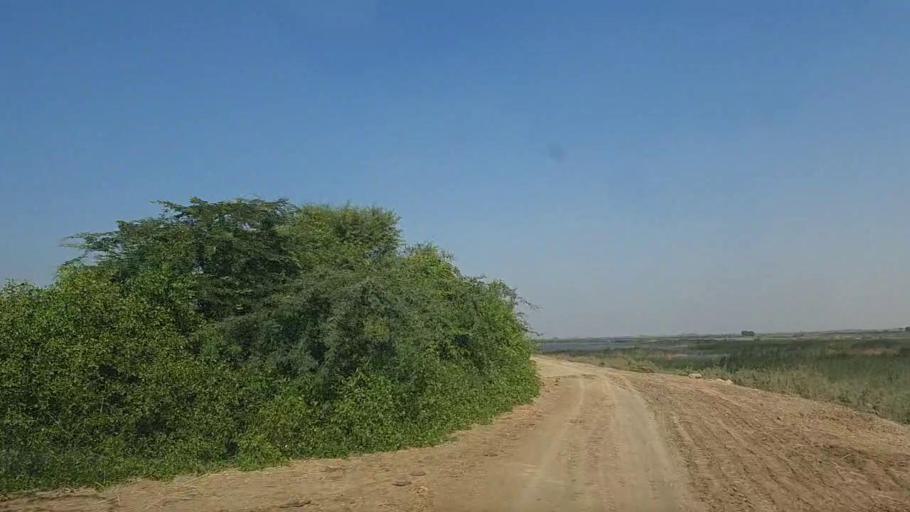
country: PK
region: Sindh
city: Daro Mehar
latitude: 24.9157
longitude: 68.0782
